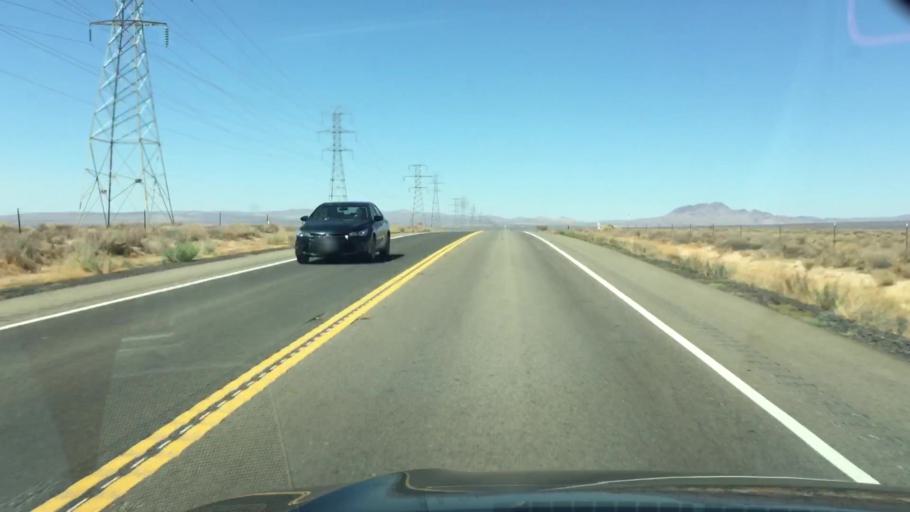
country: US
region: California
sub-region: Kern County
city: Boron
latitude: 35.1353
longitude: -117.5814
